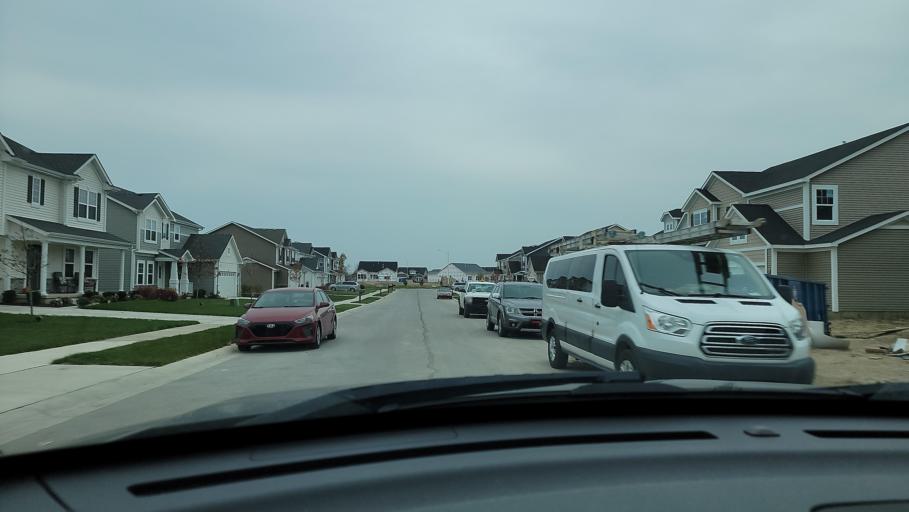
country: US
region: Indiana
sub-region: Porter County
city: South Haven
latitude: 41.5443
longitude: -87.1685
